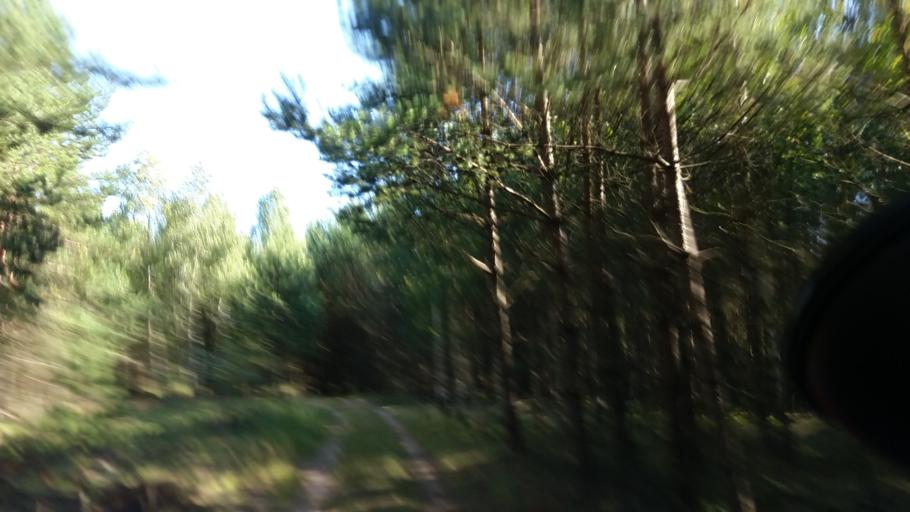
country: PL
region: West Pomeranian Voivodeship
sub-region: Powiat szczecinecki
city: Borne Sulinowo
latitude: 53.5768
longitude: 16.5189
